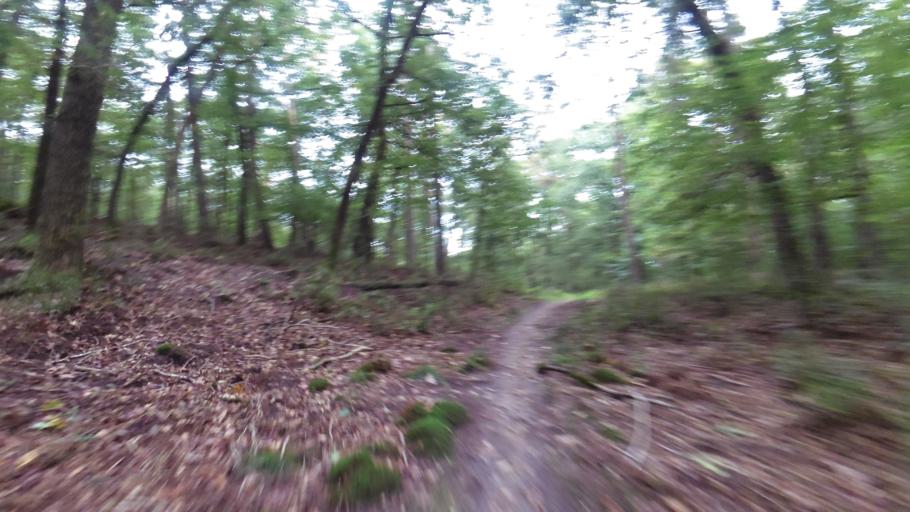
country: NL
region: Gelderland
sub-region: Gemeente Apeldoorn
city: Beekbergen
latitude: 52.1594
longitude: 5.8766
